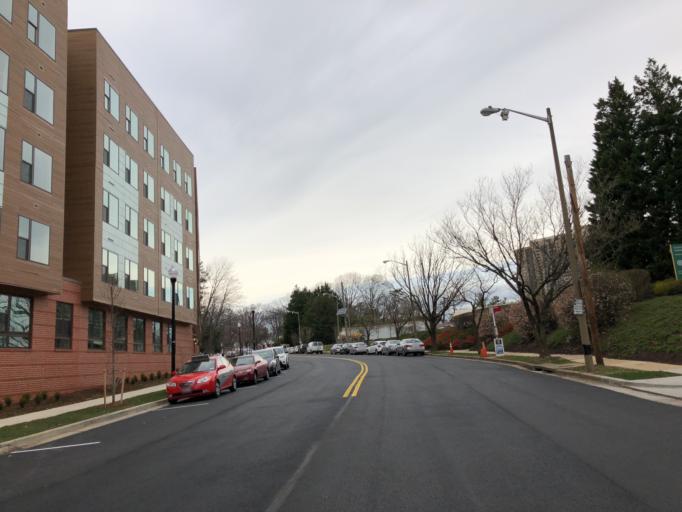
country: US
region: Virginia
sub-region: Fairfax County
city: Baileys Crossroads
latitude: 38.8386
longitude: -77.1162
